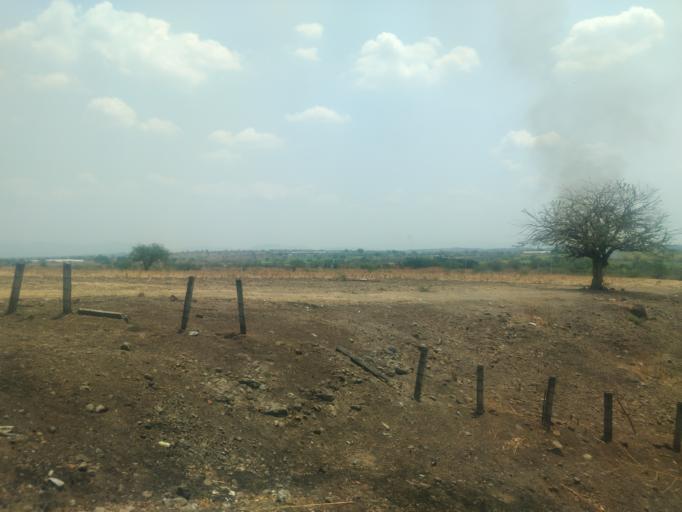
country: MX
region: Morelos
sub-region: Mazatepec
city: Cuauchichinola
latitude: 18.6363
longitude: -99.3806
